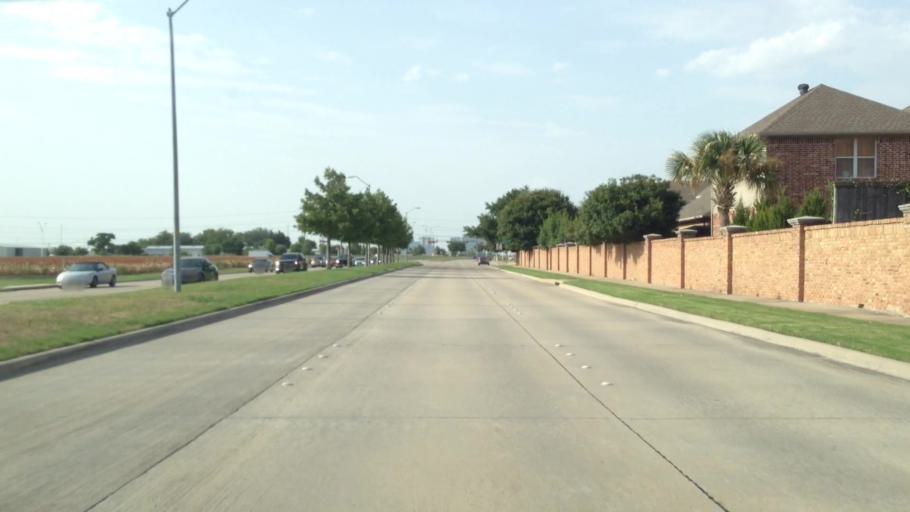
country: US
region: Texas
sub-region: Denton County
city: The Colony
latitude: 33.0524
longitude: -96.8261
